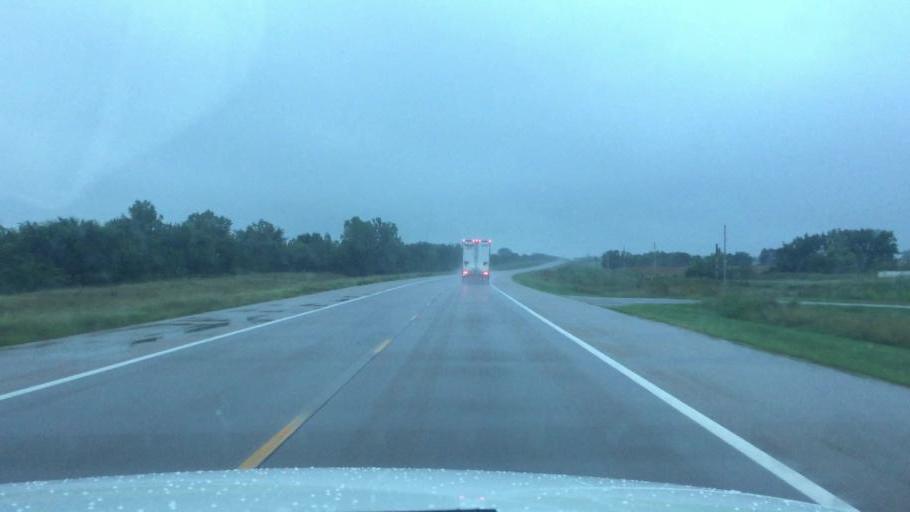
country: US
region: Kansas
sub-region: Neosho County
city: Chanute
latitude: 37.5234
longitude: -95.4712
